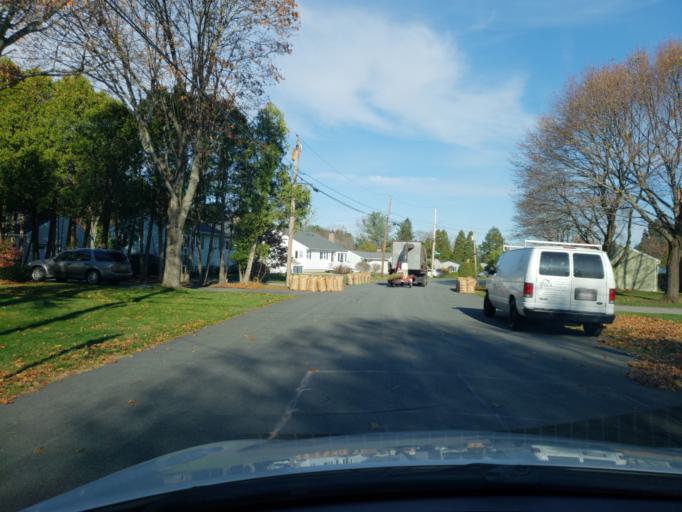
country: US
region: Massachusetts
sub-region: Essex County
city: Andover
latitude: 42.6683
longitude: -71.1272
